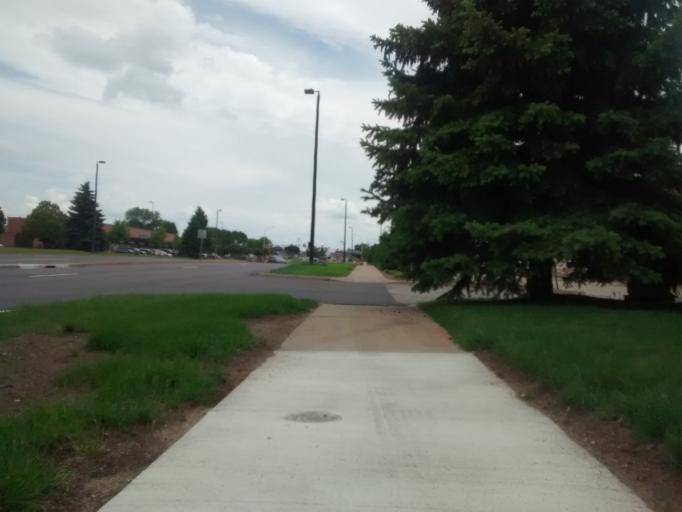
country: US
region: Minnesota
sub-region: Dakota County
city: Burnsville
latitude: 44.7499
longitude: -93.2881
